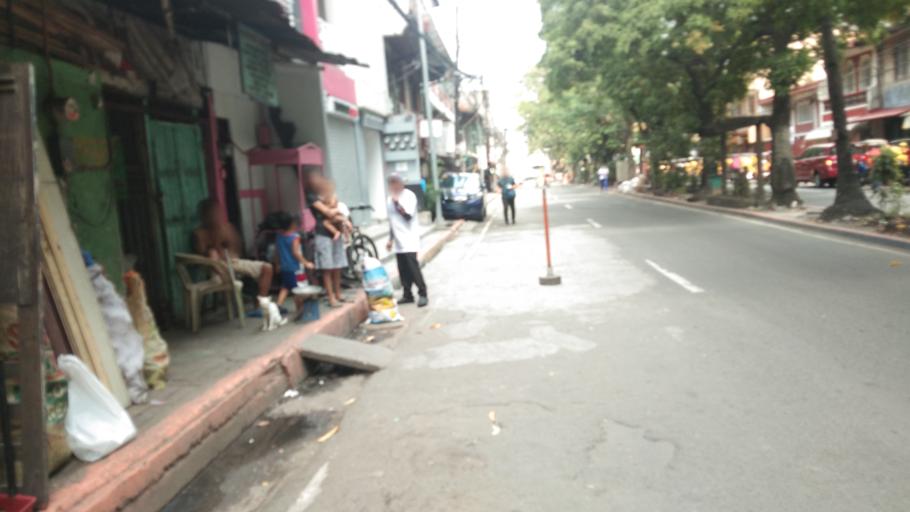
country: PH
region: Metro Manila
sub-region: City of Manila
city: Quiapo
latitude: 14.5775
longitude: 121.0012
